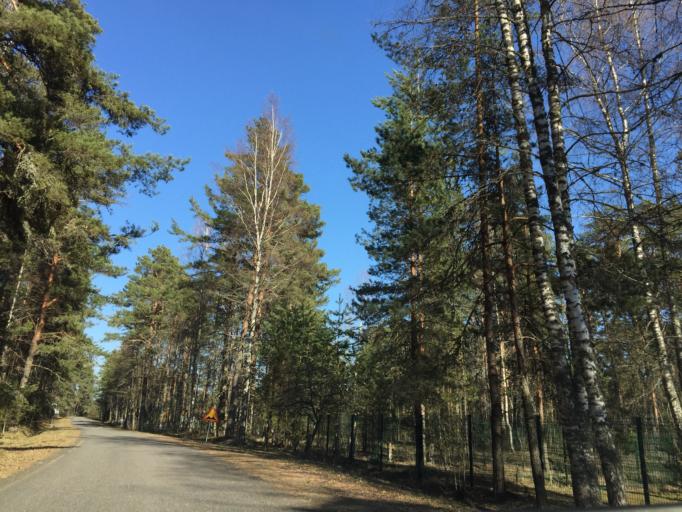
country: EE
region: Jogevamaa
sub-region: Mustvee linn
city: Mustvee
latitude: 58.9937
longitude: 27.2587
